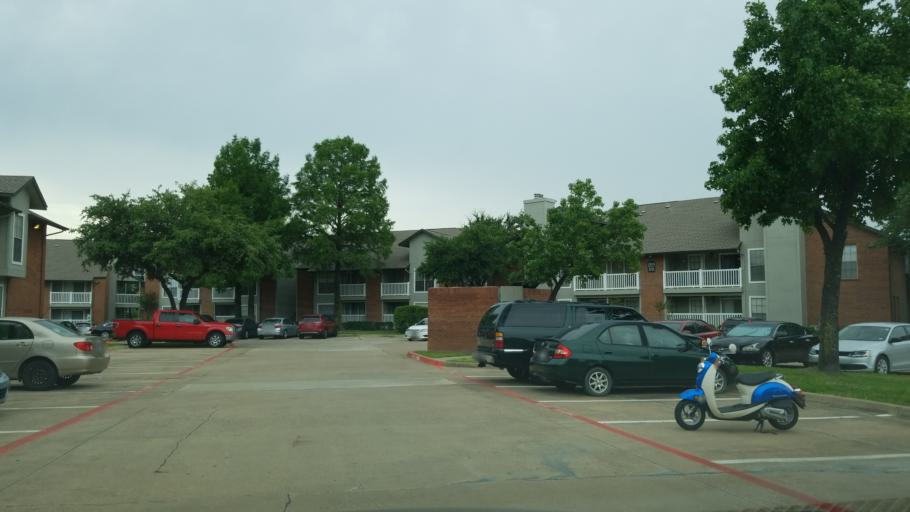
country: US
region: Texas
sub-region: Dallas County
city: Coppell
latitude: 32.9047
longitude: -96.9831
